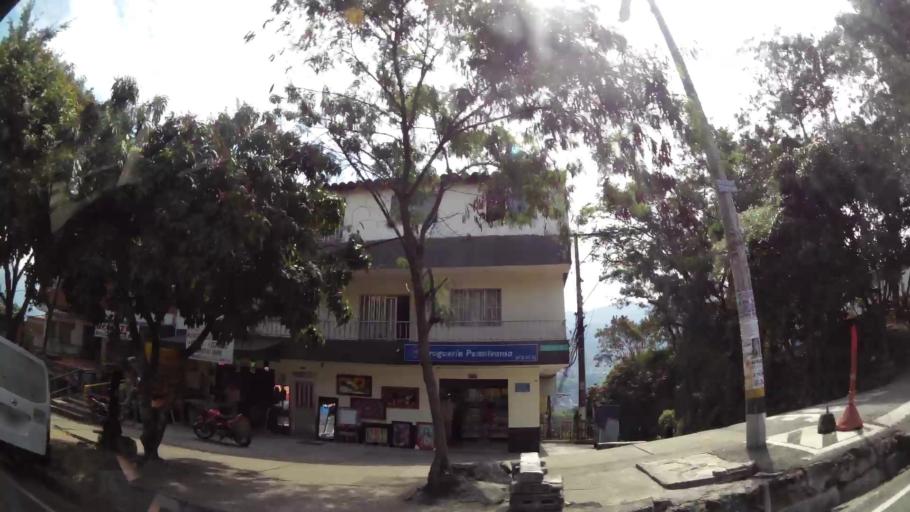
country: CO
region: Antioquia
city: Bello
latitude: 6.3094
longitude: -75.5639
